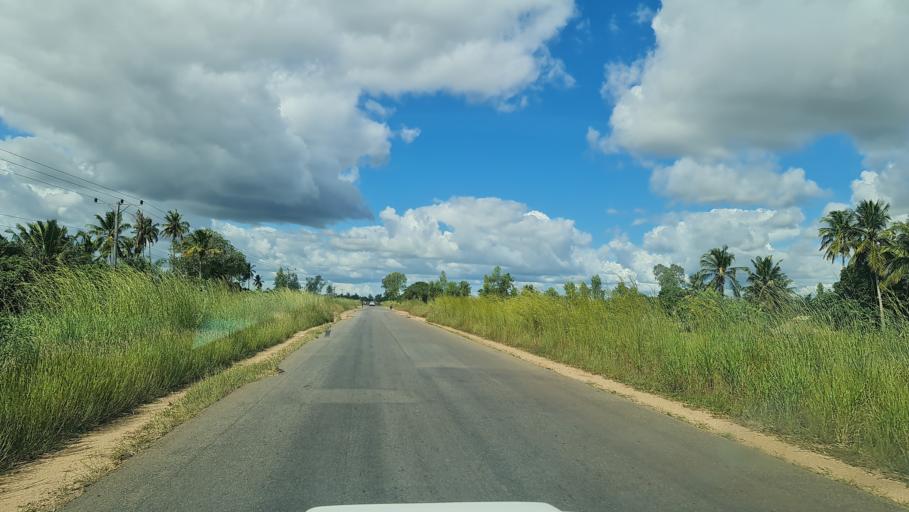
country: MZ
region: Zambezia
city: Quelimane
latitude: -17.5917
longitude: 36.7690
